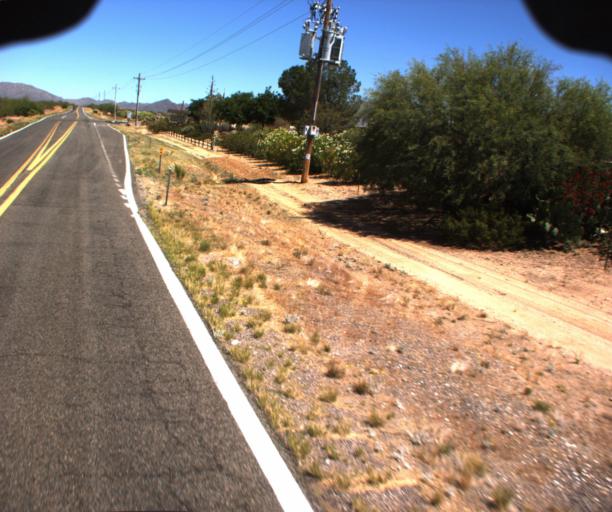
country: US
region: Arizona
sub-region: Yavapai County
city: Congress
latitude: 34.1035
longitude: -112.8311
